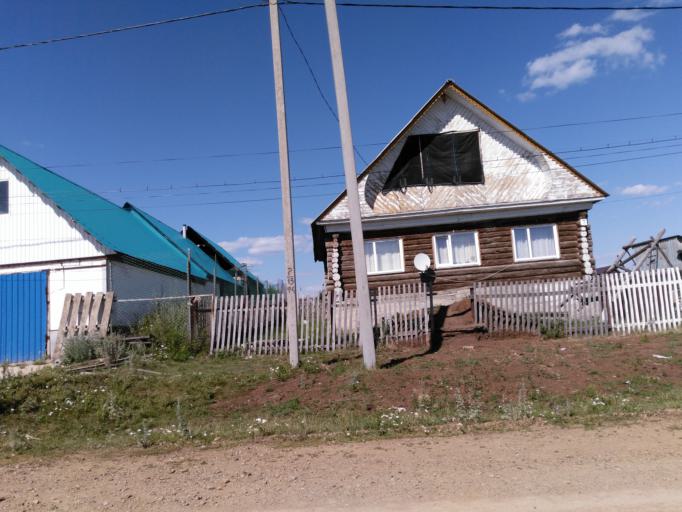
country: RU
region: Bashkortostan
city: Uchaly
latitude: 54.2929
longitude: 59.3642
